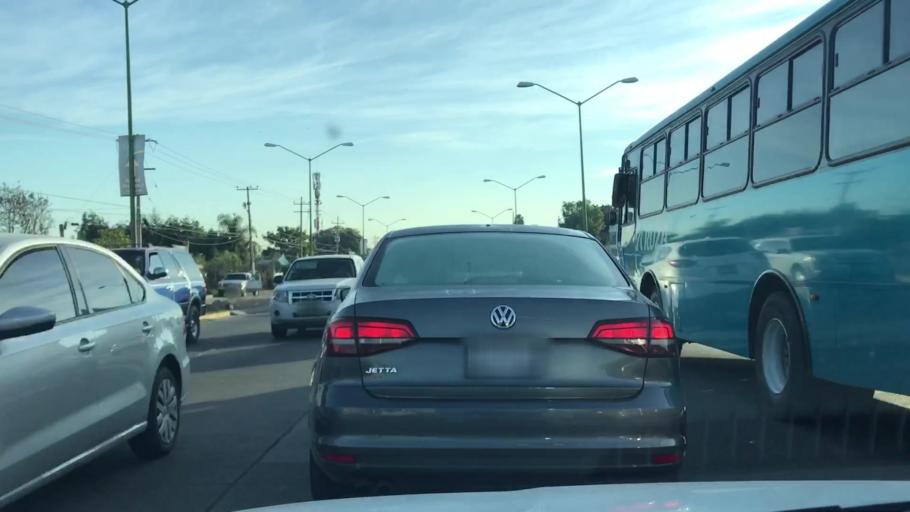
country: MX
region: Jalisco
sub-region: Tlajomulco de Zuniga
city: Palomar
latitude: 20.6254
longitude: -103.4645
